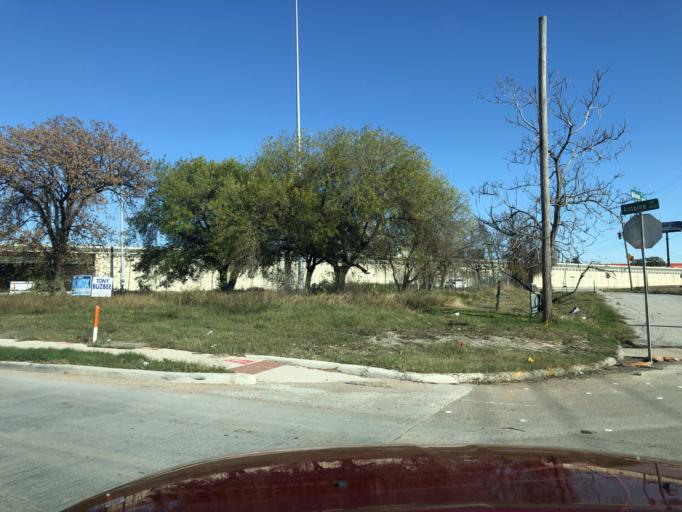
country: US
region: Texas
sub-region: Harris County
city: Spring Valley
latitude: 29.8222
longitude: -95.4737
